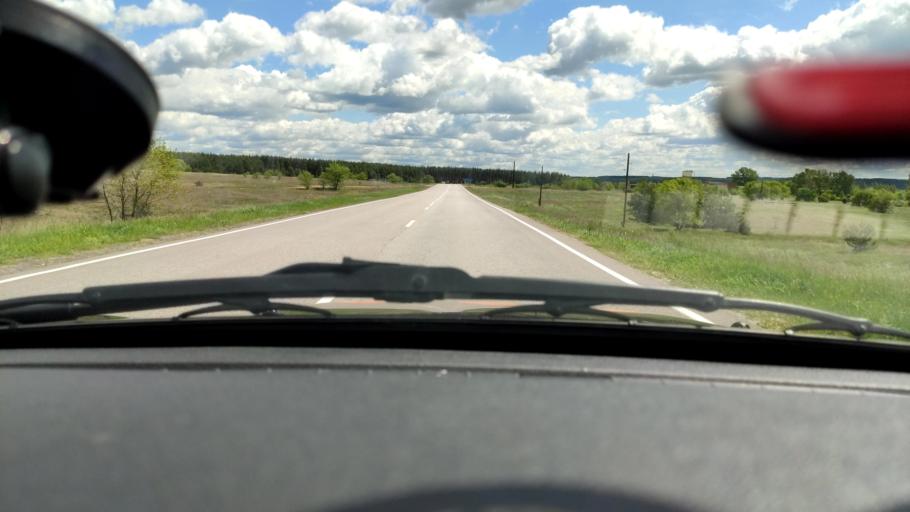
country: RU
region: Voronezj
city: Uryv-Pokrovka
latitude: 51.0516
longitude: 38.9719
